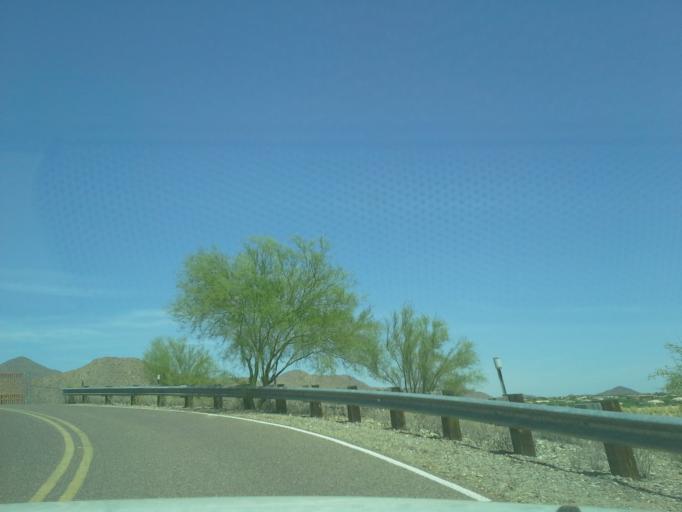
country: US
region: Arizona
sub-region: Maricopa County
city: Scottsdale
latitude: 33.5974
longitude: -111.8419
